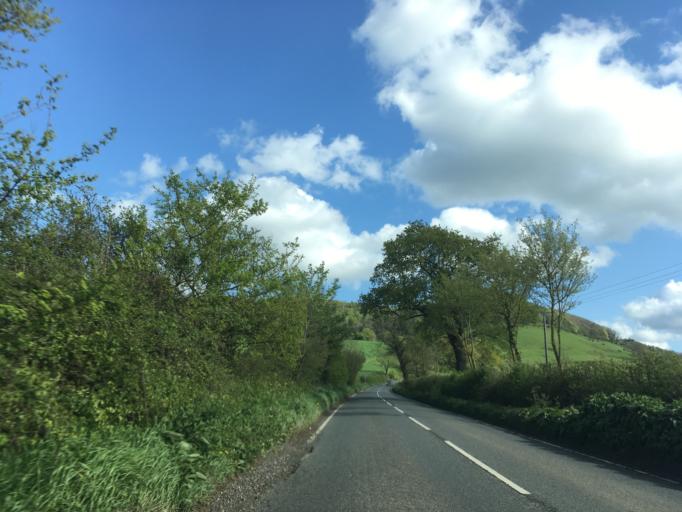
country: GB
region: England
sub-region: Gloucestershire
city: Stonehouse
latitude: 51.7204
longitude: -2.3058
